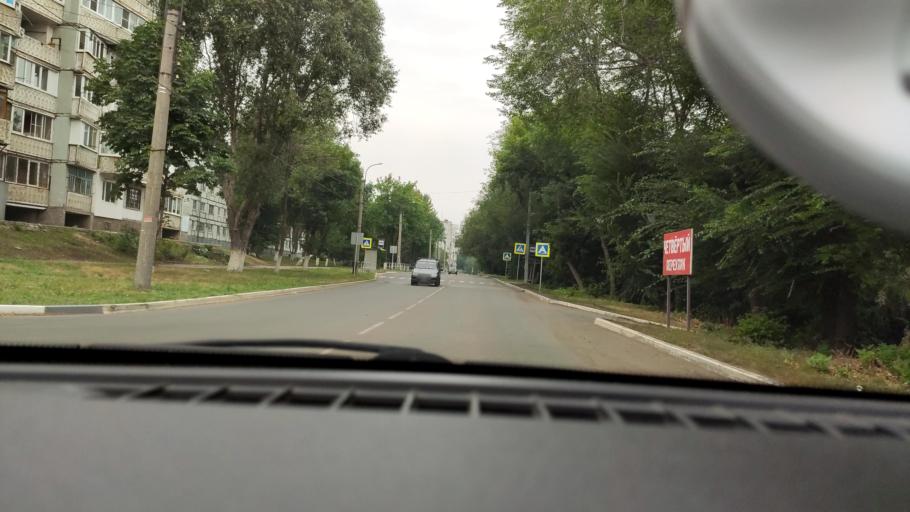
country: RU
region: Samara
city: Novokuybyshevsk
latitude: 53.0960
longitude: 49.9863
